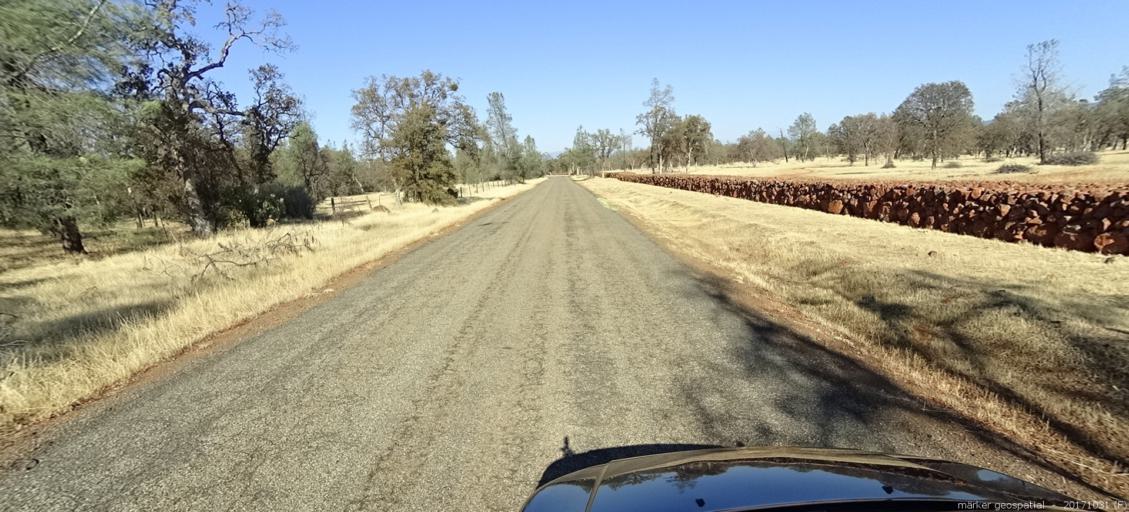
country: US
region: California
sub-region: Shasta County
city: Palo Cedro
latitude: 40.4717
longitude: -122.0905
